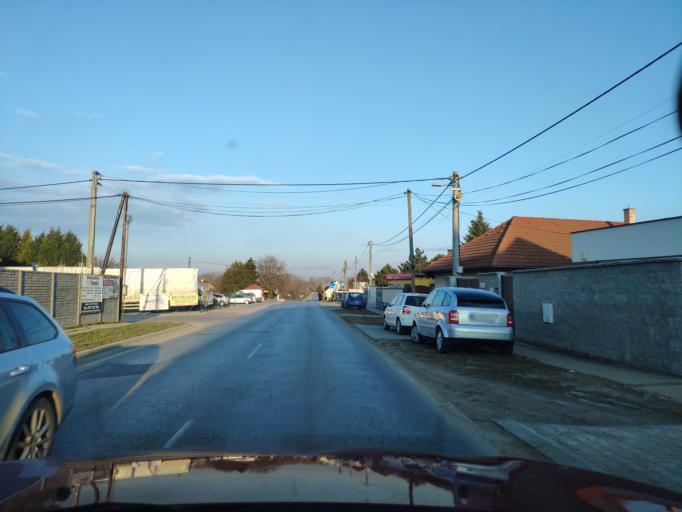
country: SK
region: Trnavsky
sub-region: Okres Galanta
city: Galanta
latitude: 48.2736
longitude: 17.8256
